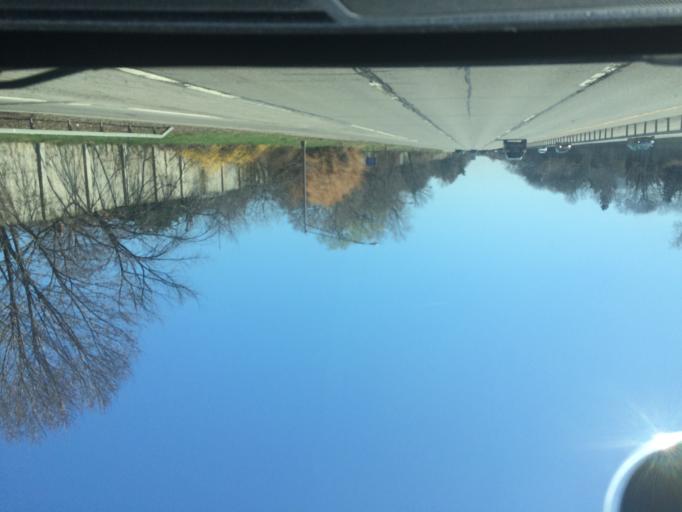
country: US
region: New York
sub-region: Monroe County
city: Brighton
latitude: 43.1361
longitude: -77.5531
